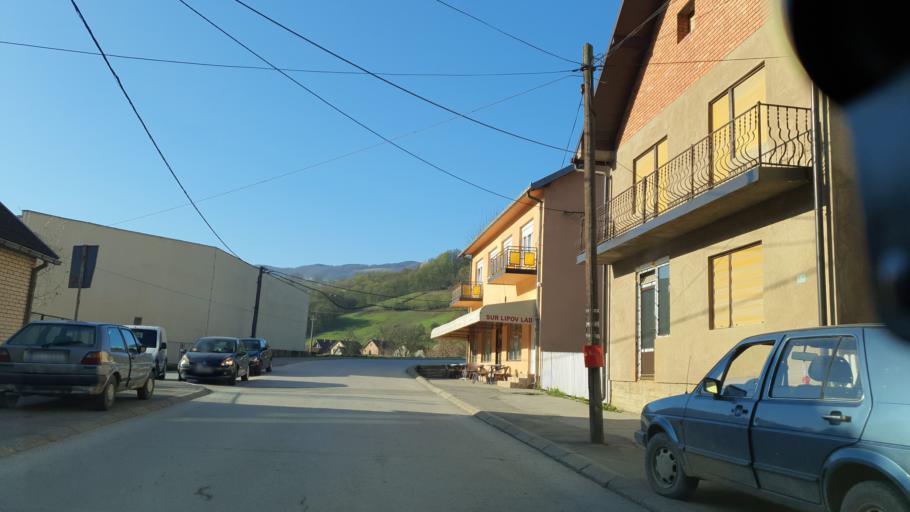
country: RS
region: Central Serbia
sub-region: Kolubarski Okrug
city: Osecina
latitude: 44.2927
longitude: 19.5401
